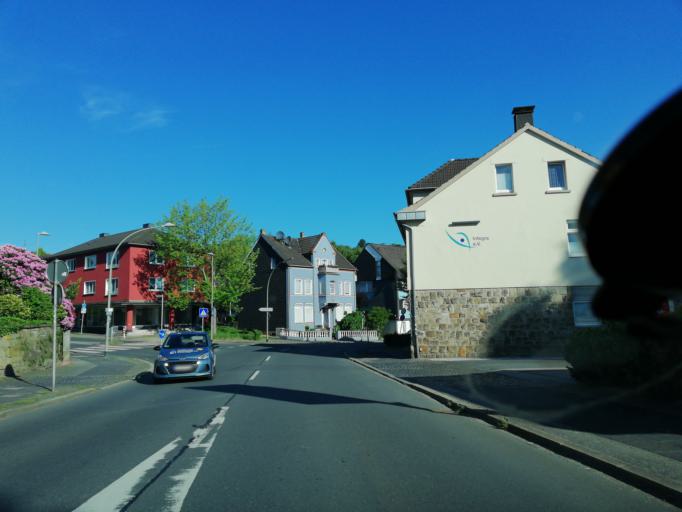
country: DE
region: North Rhine-Westphalia
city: Witten
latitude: 51.4012
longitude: 7.3458
